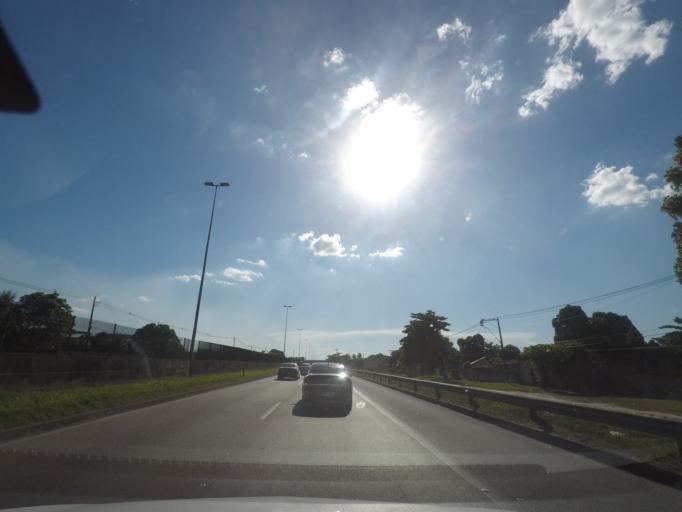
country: BR
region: Rio de Janeiro
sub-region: Petropolis
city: Petropolis
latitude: -22.6495
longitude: -43.2327
